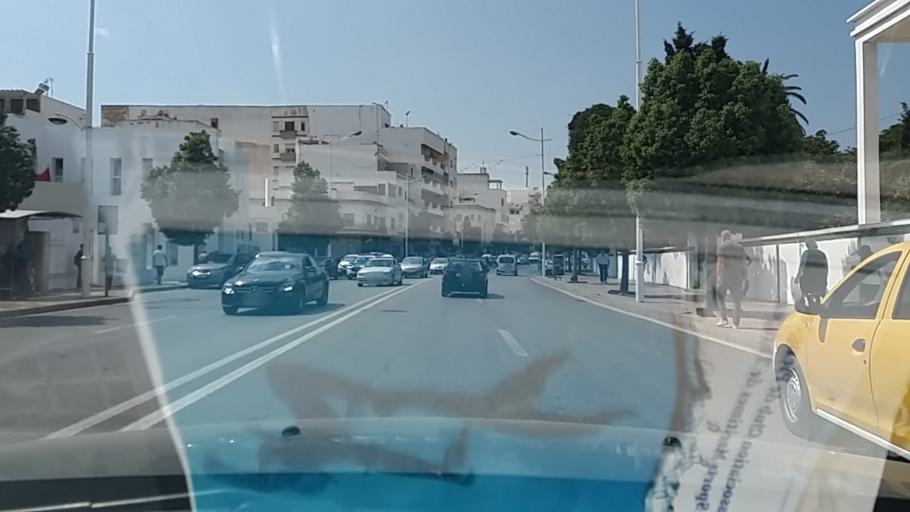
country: MA
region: Tanger-Tetouan
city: Tetouan
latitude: 35.5728
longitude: -5.3541
